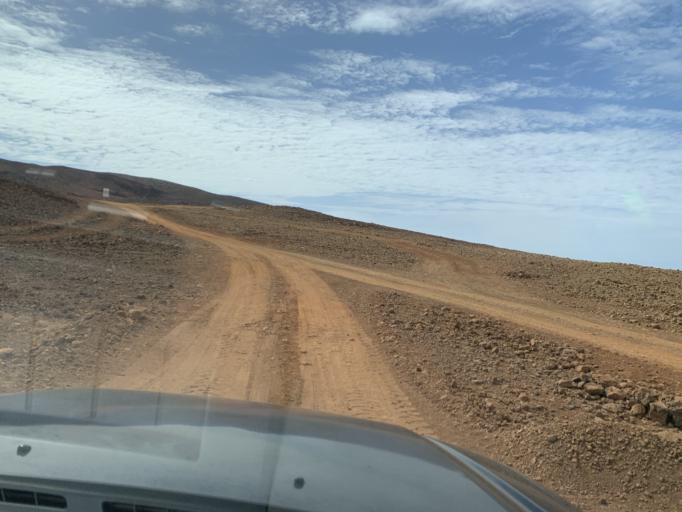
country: CV
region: Porto Novo
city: Porto Novo
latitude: 16.9650
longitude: -25.2722
